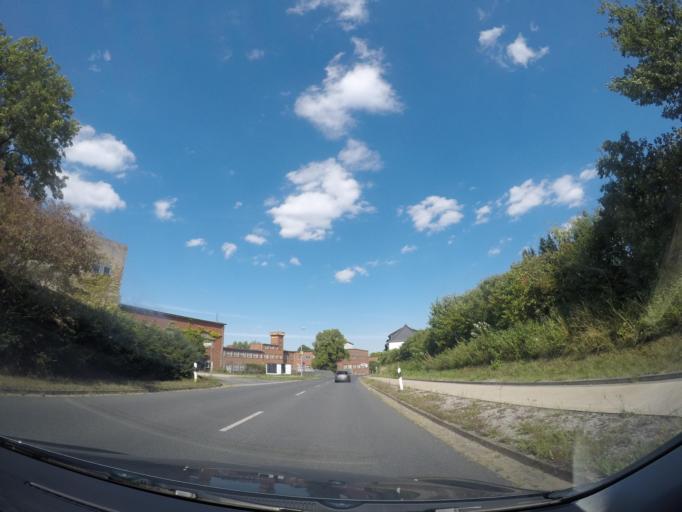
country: DE
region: Lower Saxony
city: Seesen
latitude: 51.8851
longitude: 10.1734
